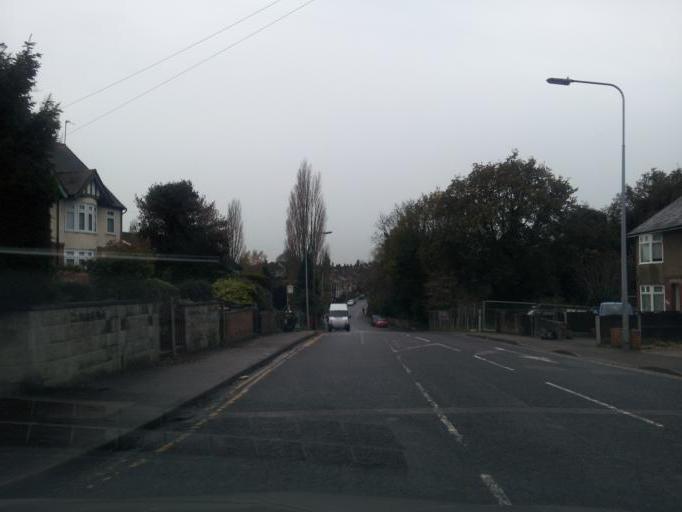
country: GB
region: England
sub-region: Essex
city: Colchester
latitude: 51.8761
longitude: 0.9220
